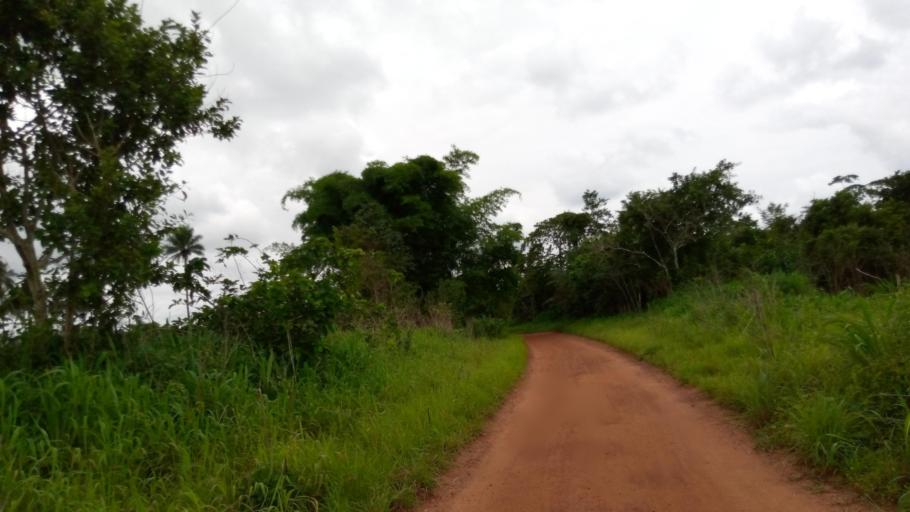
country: SL
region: Southern Province
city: Moyamba
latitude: 8.1958
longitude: -12.5454
